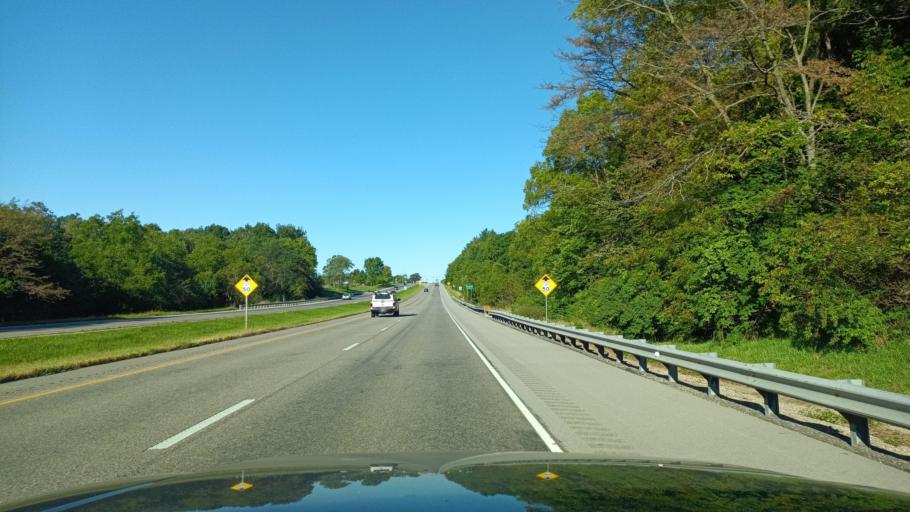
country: US
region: Illinois
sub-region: Warren County
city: Monmouth
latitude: 40.9241
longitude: -90.6232
